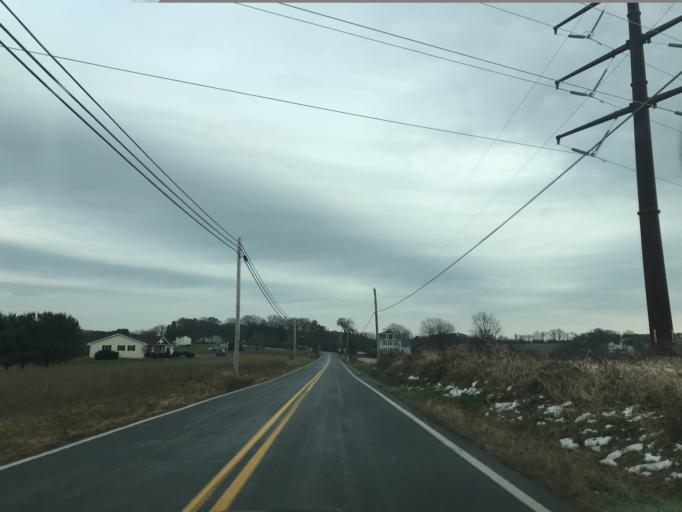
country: US
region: Pennsylvania
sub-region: York County
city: Susquehanna Trails
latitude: 39.6904
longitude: -76.3863
